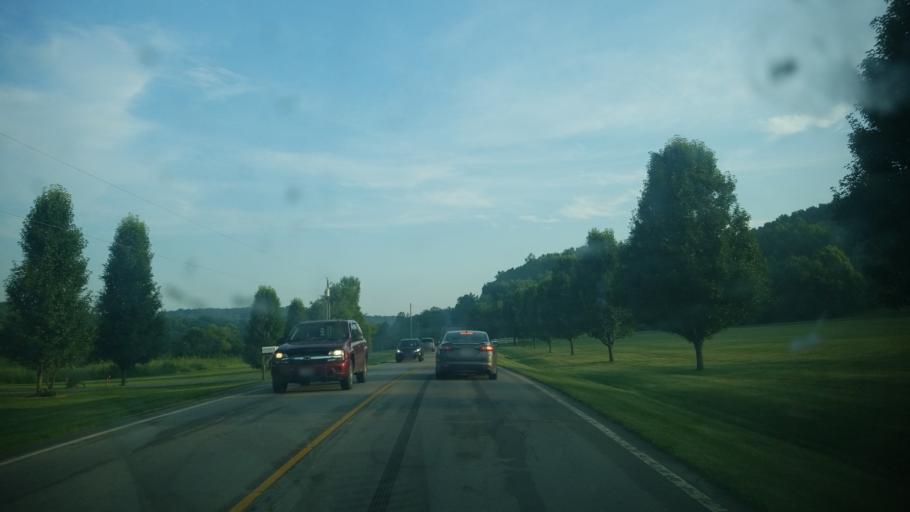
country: US
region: Ohio
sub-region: Adams County
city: Peebles
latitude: 38.8828
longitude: -83.4572
